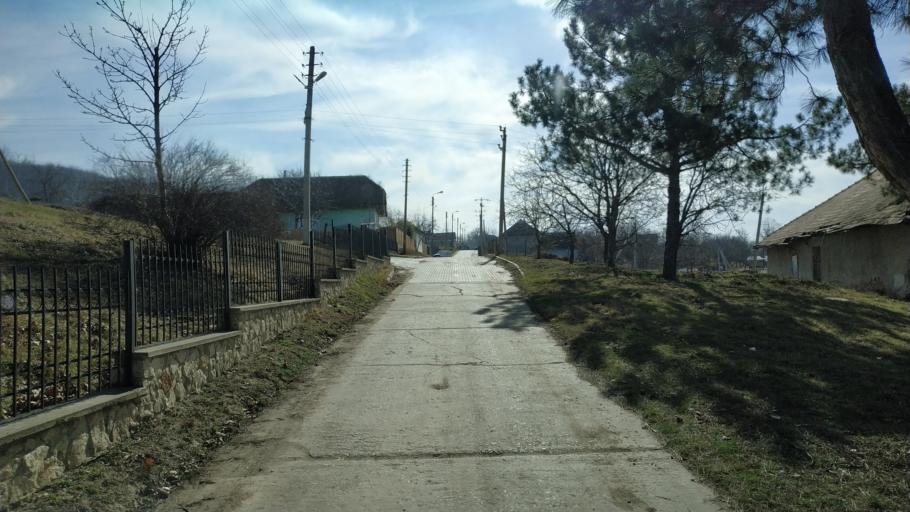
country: MD
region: Nisporeni
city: Nisporeni
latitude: 47.0784
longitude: 28.2621
